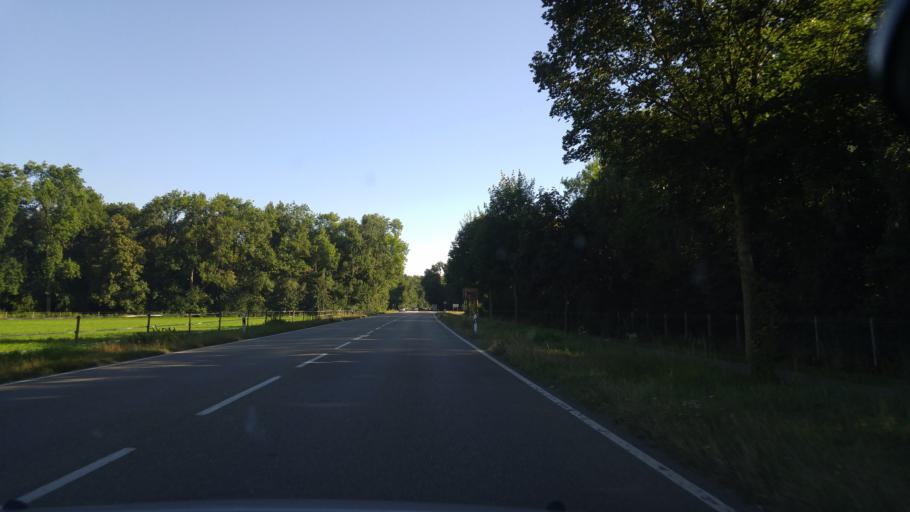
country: DE
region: Bavaria
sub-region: Swabia
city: Guenzburg
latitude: 48.4726
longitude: 10.2842
